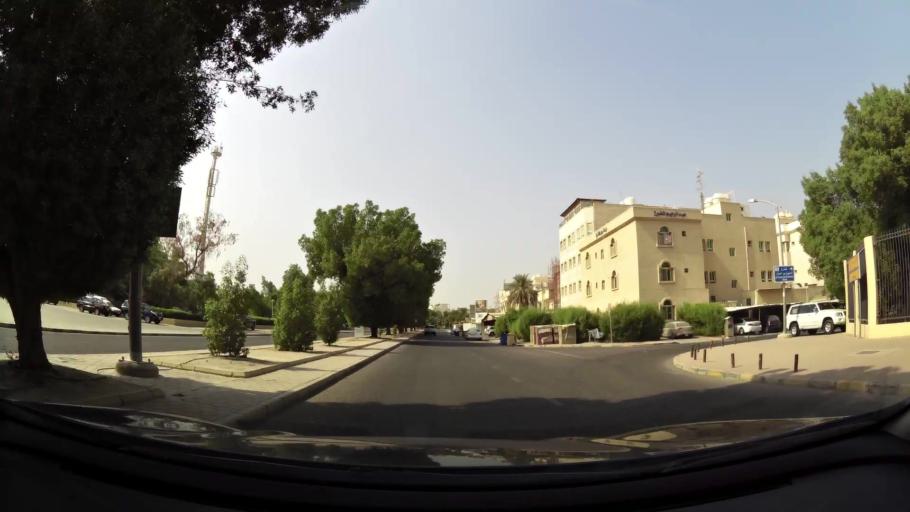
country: KW
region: Al Asimah
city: Ad Dasmah
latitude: 29.3509
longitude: 48.0169
